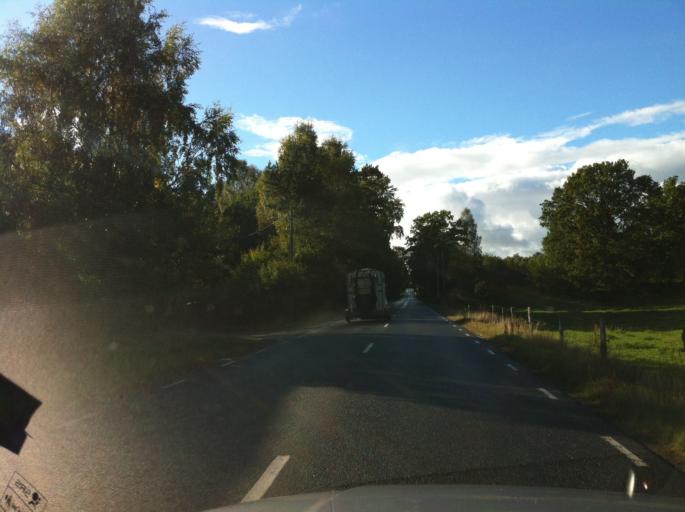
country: SE
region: Skane
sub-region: Hoors Kommun
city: Hoeoer
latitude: 56.0203
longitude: 13.4968
